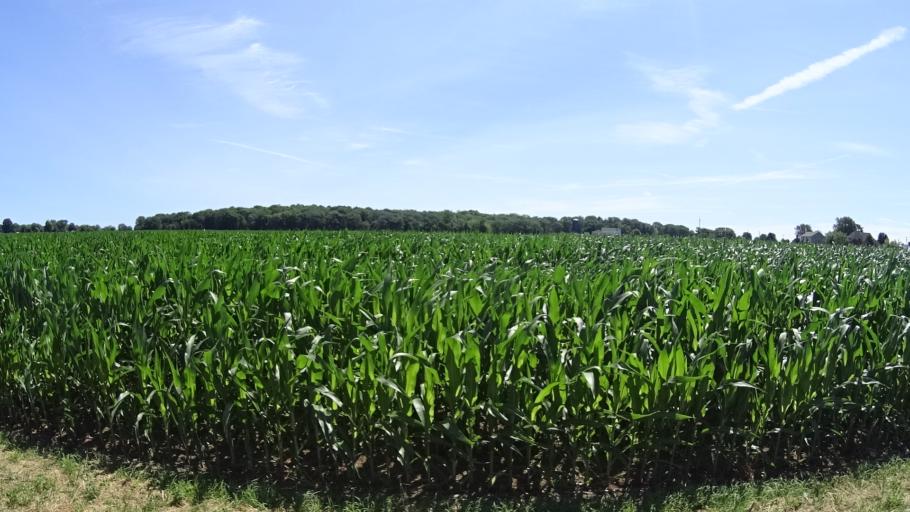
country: US
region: Ohio
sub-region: Ottawa County
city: Port Clinton
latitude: 41.4395
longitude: -82.8528
